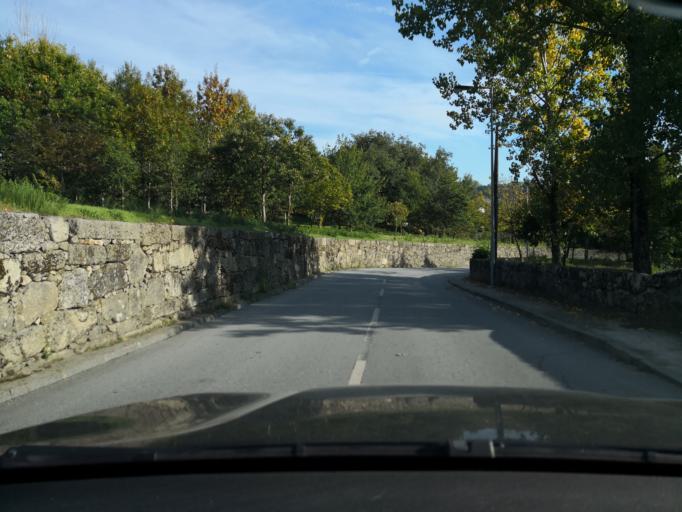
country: PT
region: Vila Real
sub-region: Vila Real
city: Vila Real
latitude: 41.3208
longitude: -7.7428
